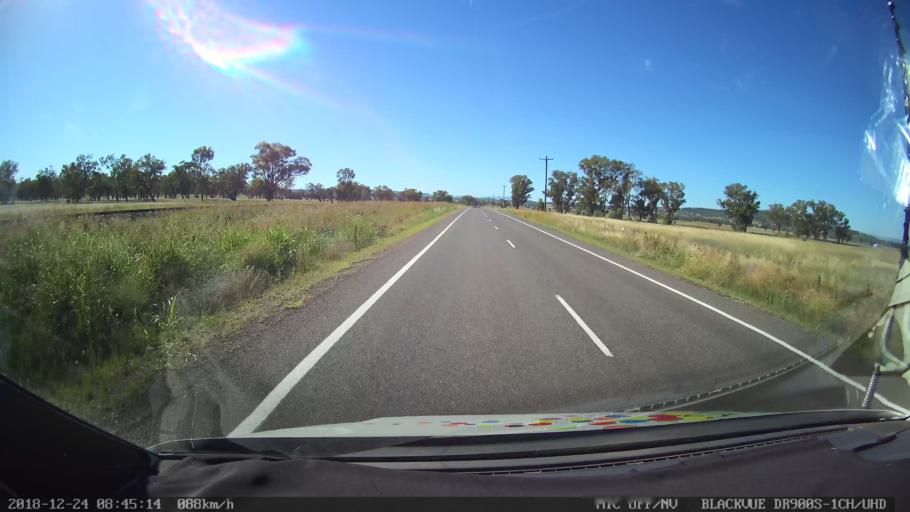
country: AU
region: New South Wales
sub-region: Liverpool Plains
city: Quirindi
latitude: -31.4123
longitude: 150.6512
